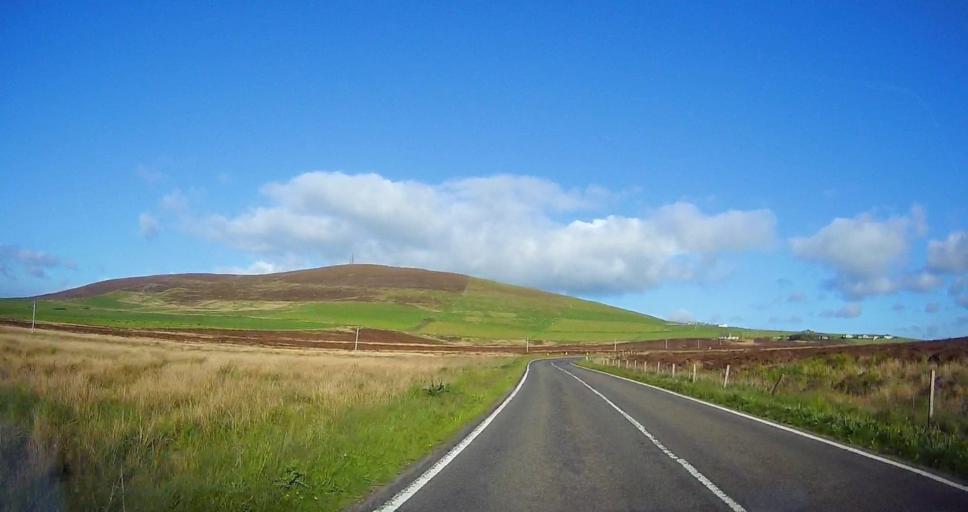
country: GB
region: Scotland
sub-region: Orkney Islands
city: Orkney
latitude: 58.9878
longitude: -3.0528
